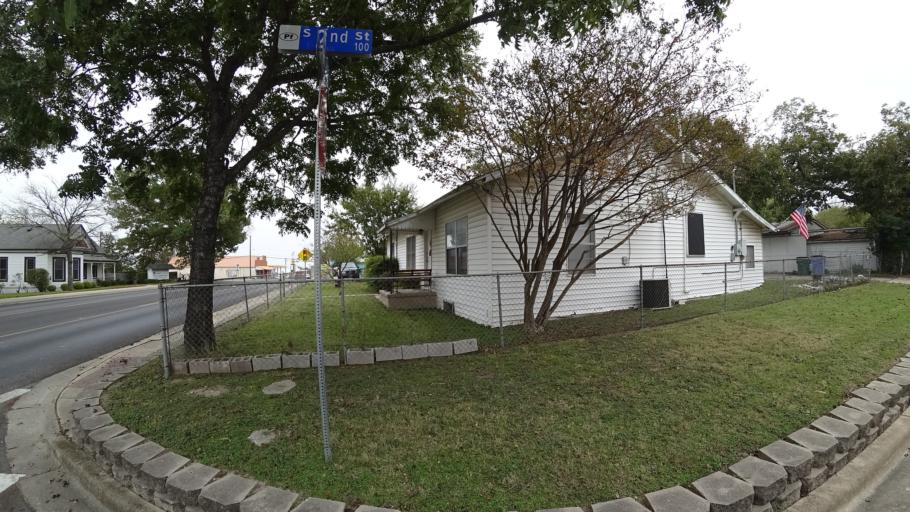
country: US
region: Texas
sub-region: Travis County
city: Pflugerville
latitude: 30.4402
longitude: -97.6219
